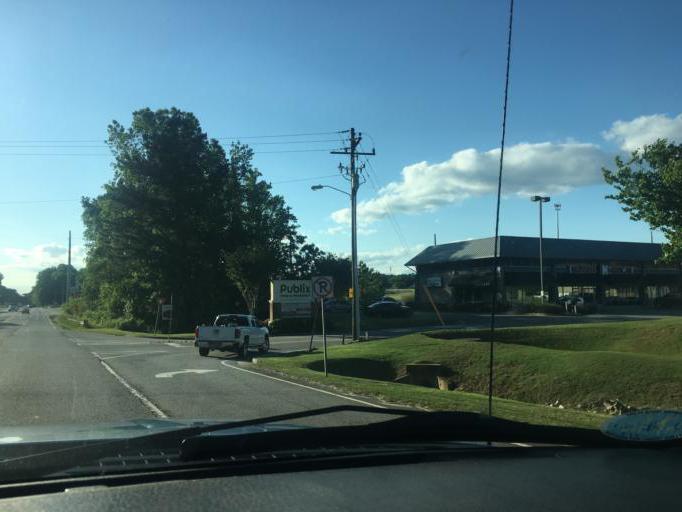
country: US
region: Georgia
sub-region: Forsyth County
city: Cumming
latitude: 34.2565
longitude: -84.0721
